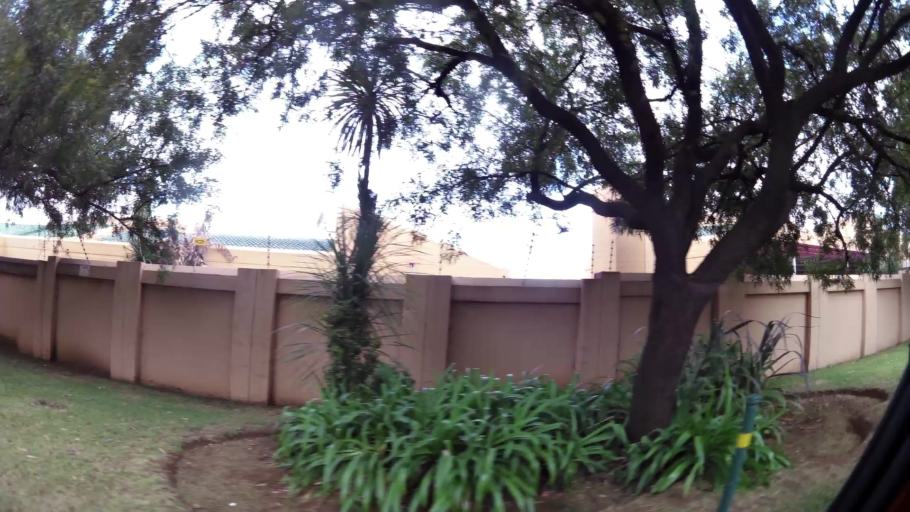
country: ZA
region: Gauteng
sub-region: Sedibeng District Municipality
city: Vanderbijlpark
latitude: -26.7368
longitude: 27.8510
